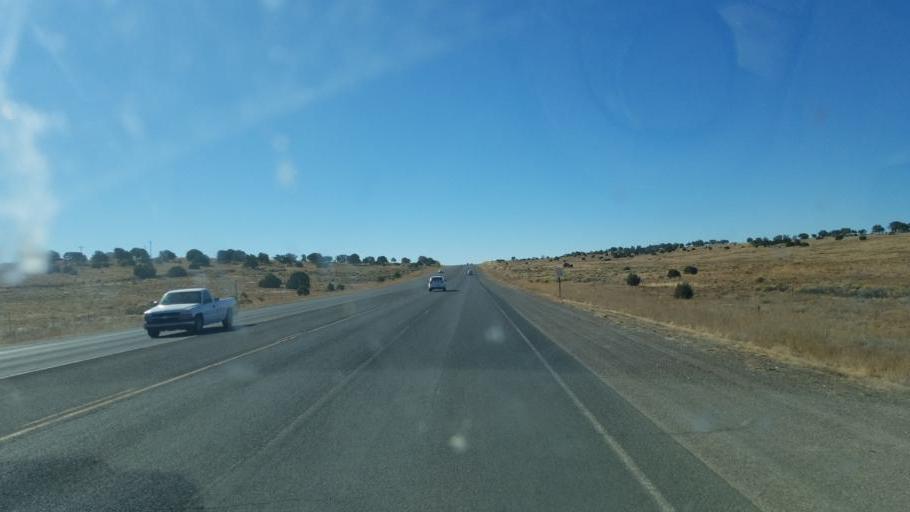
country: US
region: Arizona
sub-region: Apache County
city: Window Rock
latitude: 35.7062
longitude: -109.0631
